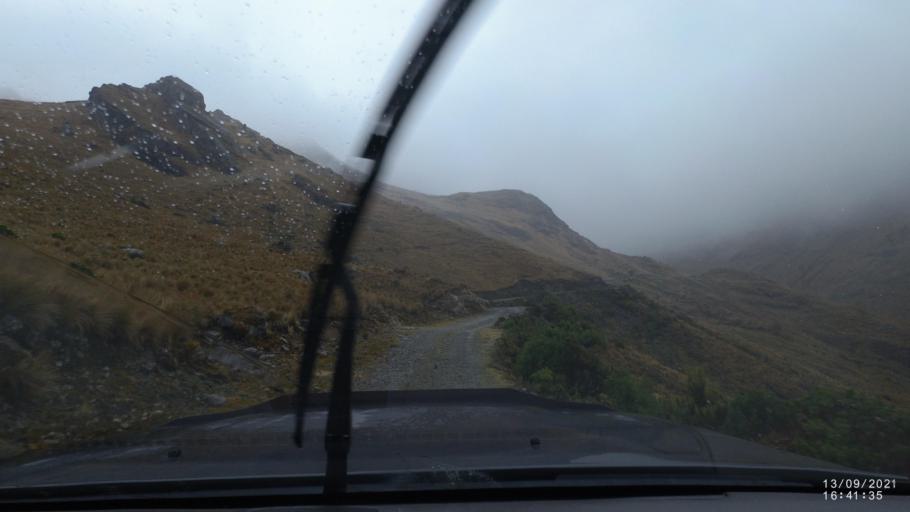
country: BO
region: Cochabamba
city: Colomi
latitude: -17.2844
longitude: -65.7119
